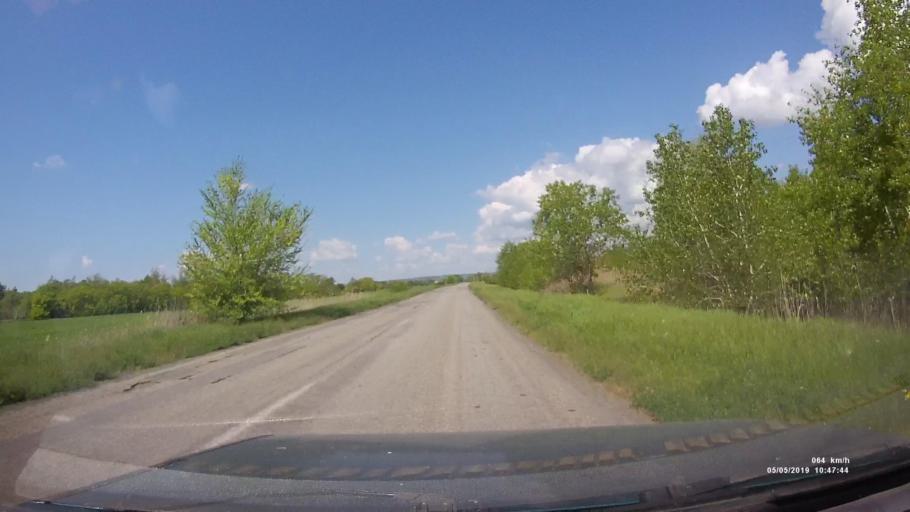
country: RU
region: Rostov
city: Ust'-Donetskiy
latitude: 47.6396
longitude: 40.8289
